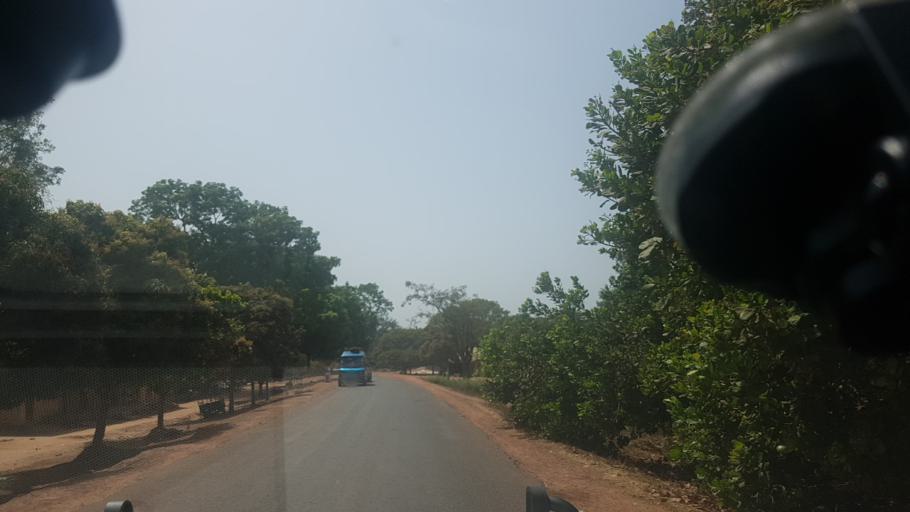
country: GW
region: Cacheu
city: Cacheu
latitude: 12.4130
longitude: -16.0742
